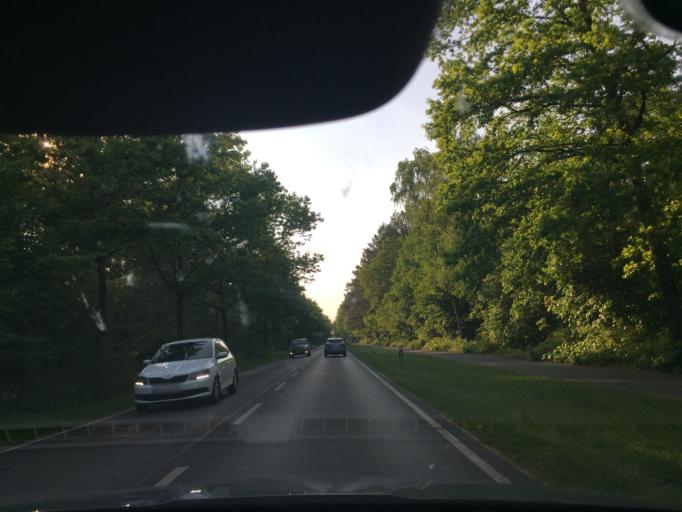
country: DE
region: Berlin
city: Grunau
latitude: 52.4026
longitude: 13.5956
